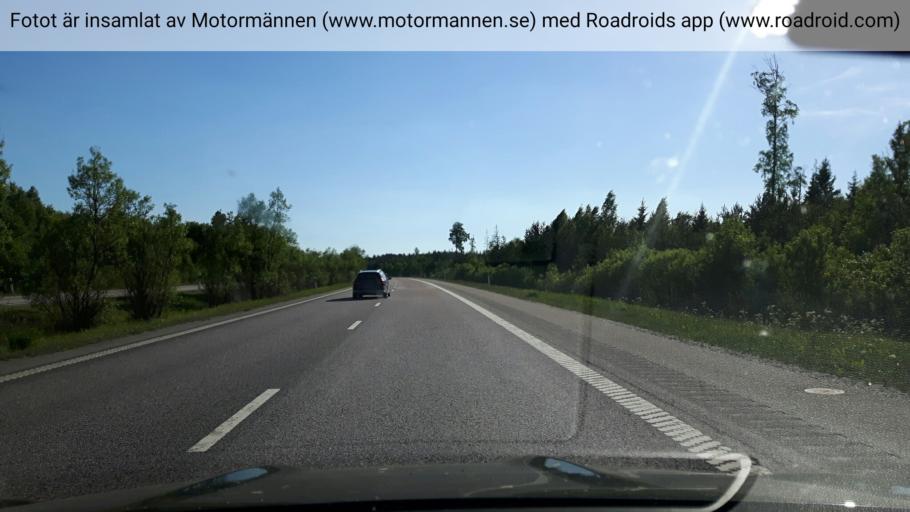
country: SE
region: Stockholm
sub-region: Norrtalje Kommun
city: Rimbo
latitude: 59.6670
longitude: 18.3828
